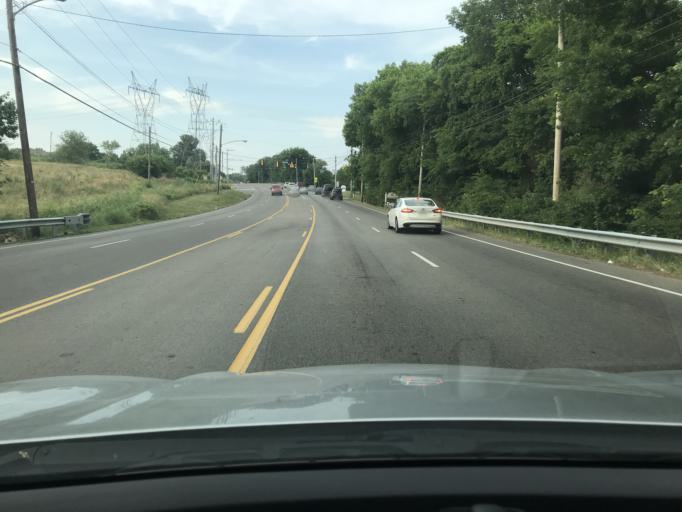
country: US
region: Tennessee
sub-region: Davidson County
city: Goodlettsville
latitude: 36.2972
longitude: -86.7241
